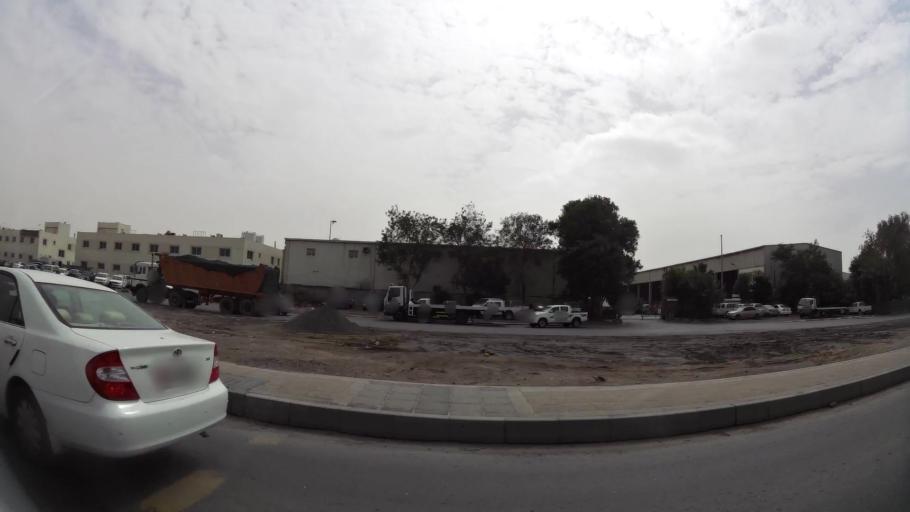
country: AE
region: Abu Dhabi
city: Abu Dhabi
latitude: 24.3458
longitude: 54.5095
